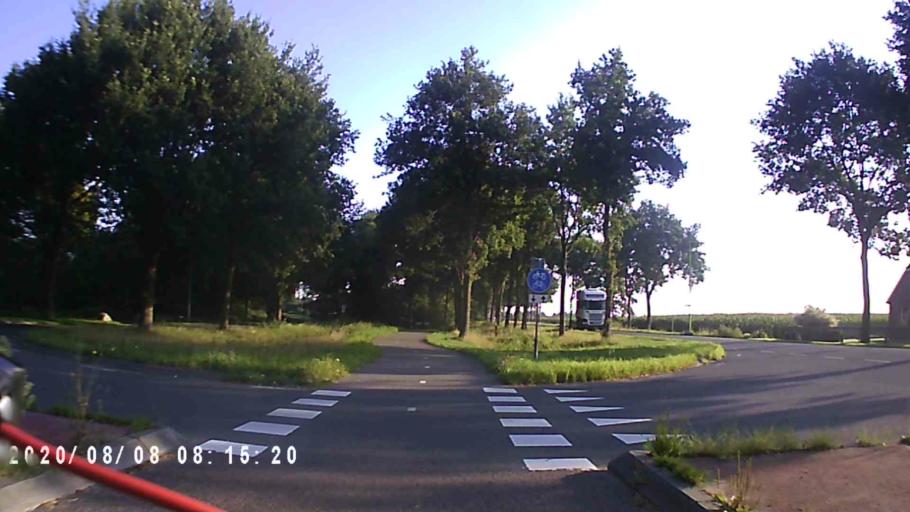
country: NL
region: Groningen
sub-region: Gemeente Leek
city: Leek
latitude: 53.0961
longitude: 6.3413
